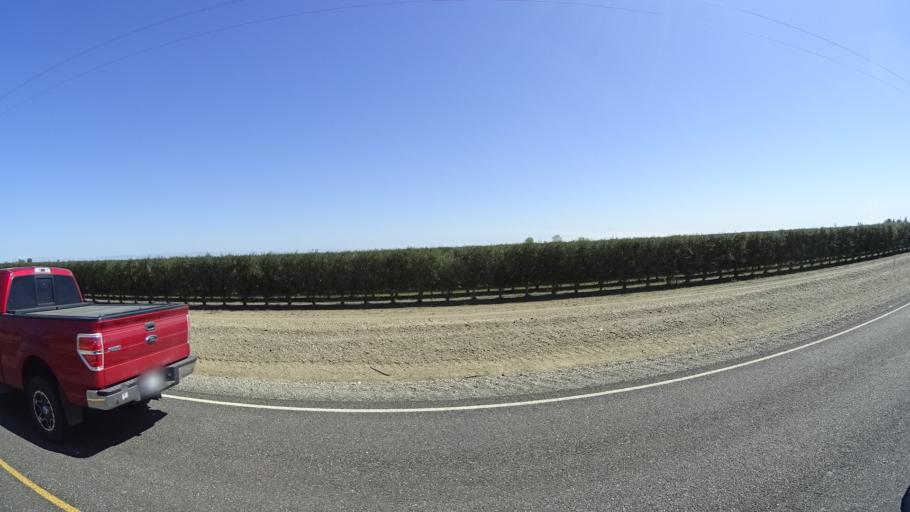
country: US
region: California
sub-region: Glenn County
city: Willows
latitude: 39.6198
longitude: -122.2500
